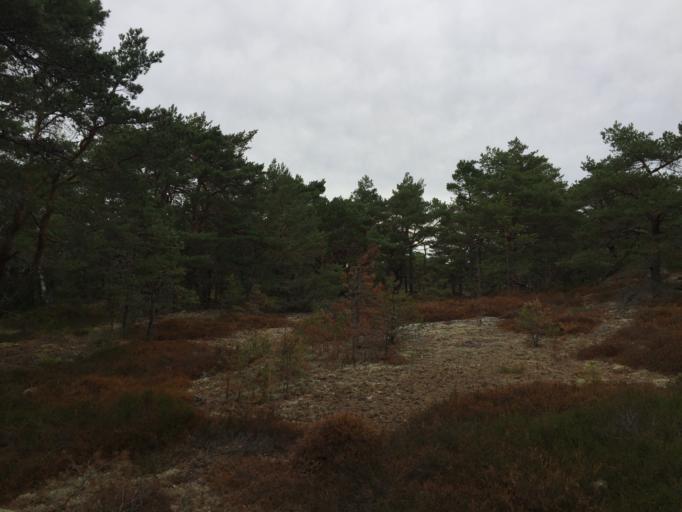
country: NO
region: Ostfold
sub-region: Hvaler
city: Skjaerhalden
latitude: 59.0564
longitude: 11.0380
